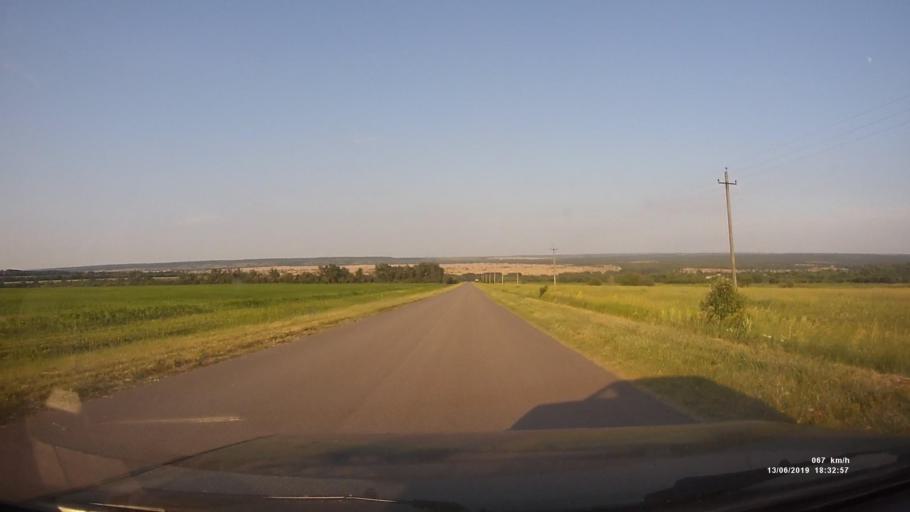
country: RU
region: Rostov
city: Kazanskaya
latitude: 49.8703
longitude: 41.3748
